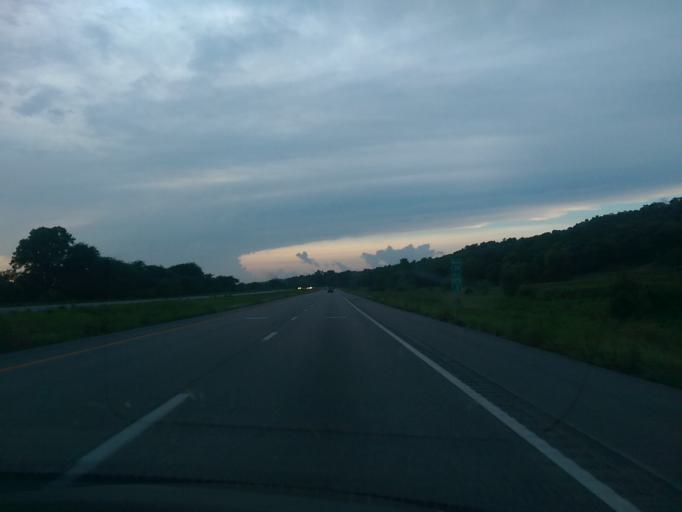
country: US
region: Missouri
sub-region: Atchison County
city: Rock Port
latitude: 40.3365
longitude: -95.4993
